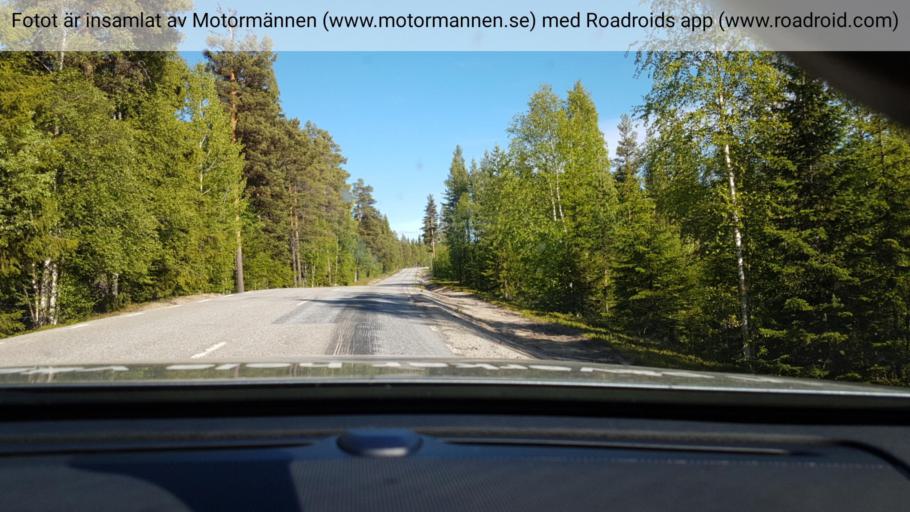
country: SE
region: Vaesterbotten
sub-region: Norsjo Kommun
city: Norsjoe
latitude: 64.6956
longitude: 19.1847
